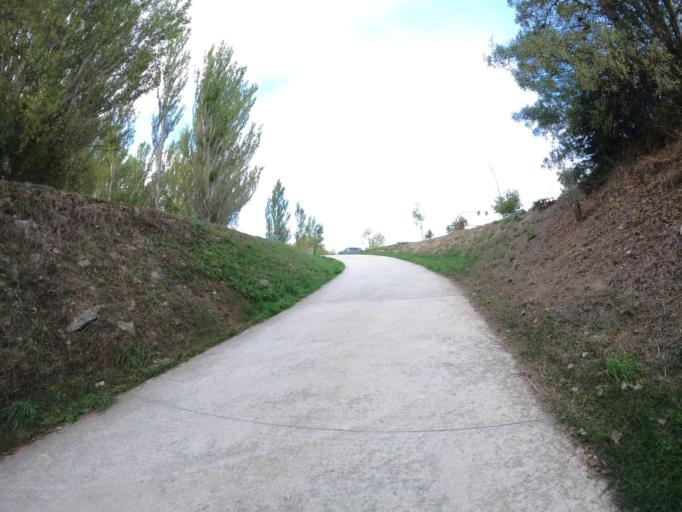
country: ES
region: Navarre
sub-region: Provincia de Navarra
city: Cizur Mayor
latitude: 42.8033
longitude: -1.7000
